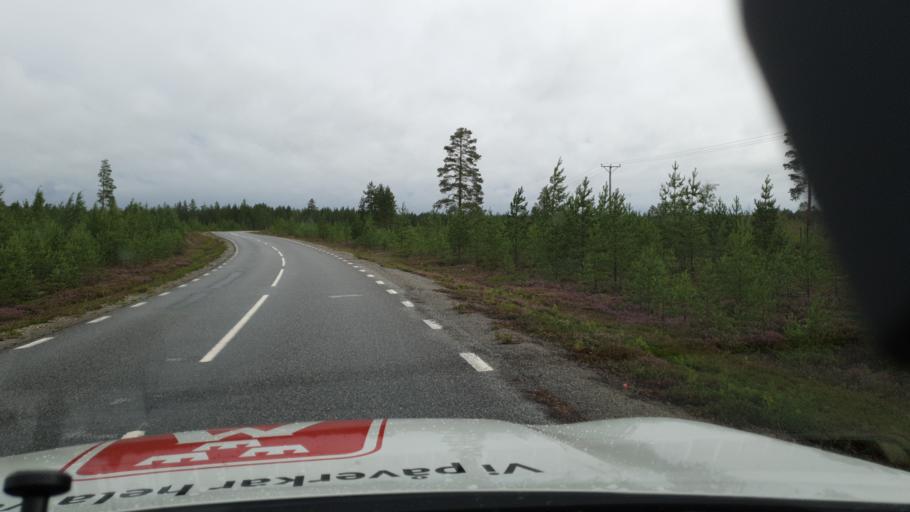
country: SE
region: Vaesterbotten
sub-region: Umea Kommun
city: Saevar
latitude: 63.9709
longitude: 20.5074
